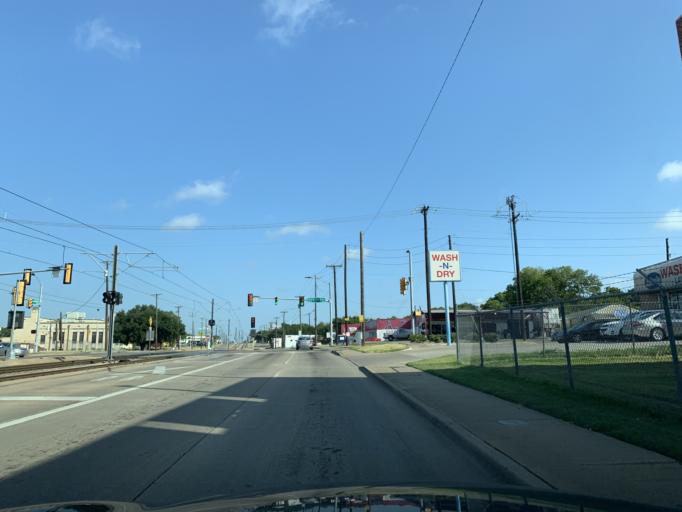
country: US
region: Texas
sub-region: Dallas County
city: Dallas
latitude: 32.6965
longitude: -96.7939
